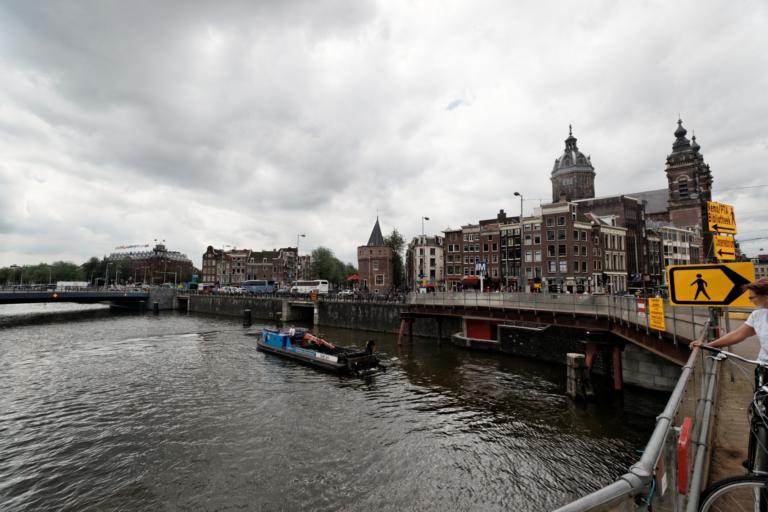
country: NL
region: North Holland
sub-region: Gemeente Amsterdam
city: Amsterdam
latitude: 52.3772
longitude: 4.9028
